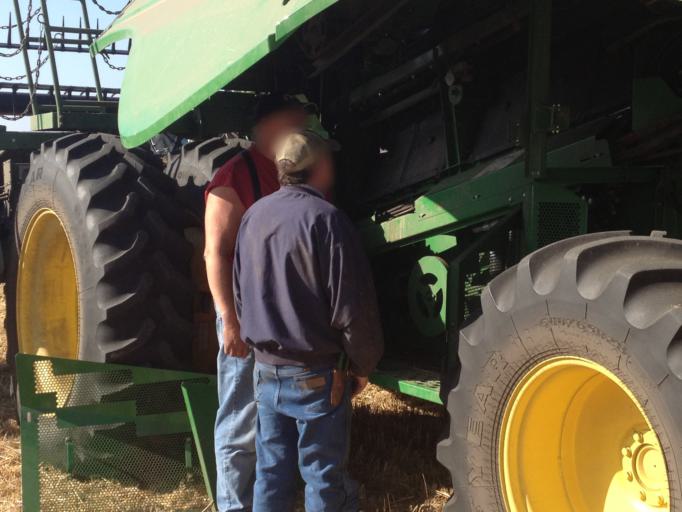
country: US
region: North Dakota
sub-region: McLean County
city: Garrison
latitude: 47.7180
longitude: -101.7962
